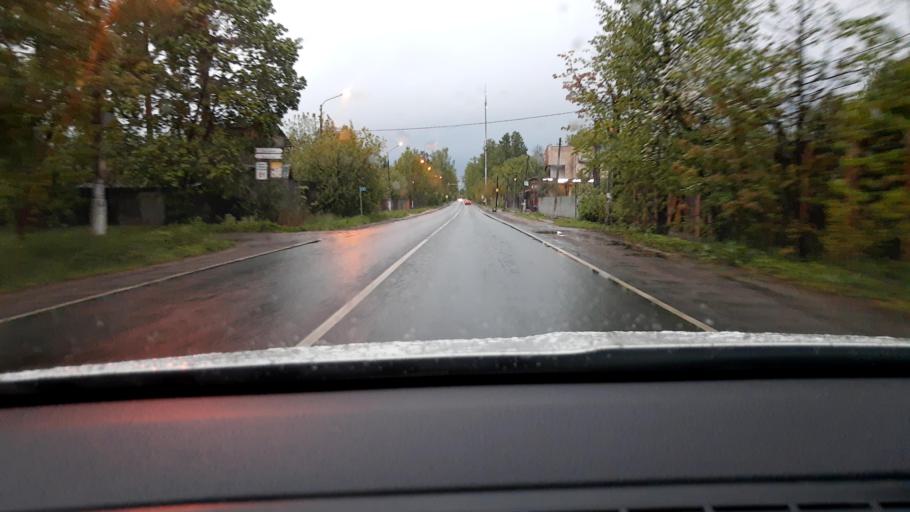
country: RU
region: Moskovskaya
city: Zagoryanskiy
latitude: 55.9171
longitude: 37.9157
